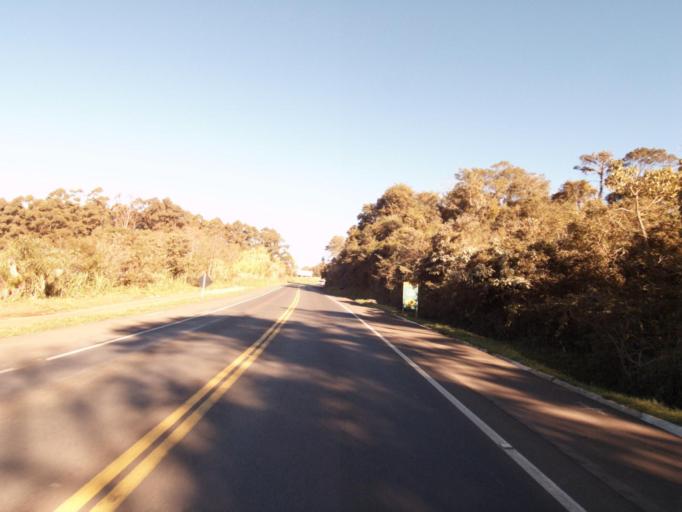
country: BR
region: Santa Catarina
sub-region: Chapeco
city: Chapeco
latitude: -26.9764
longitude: -52.5886
